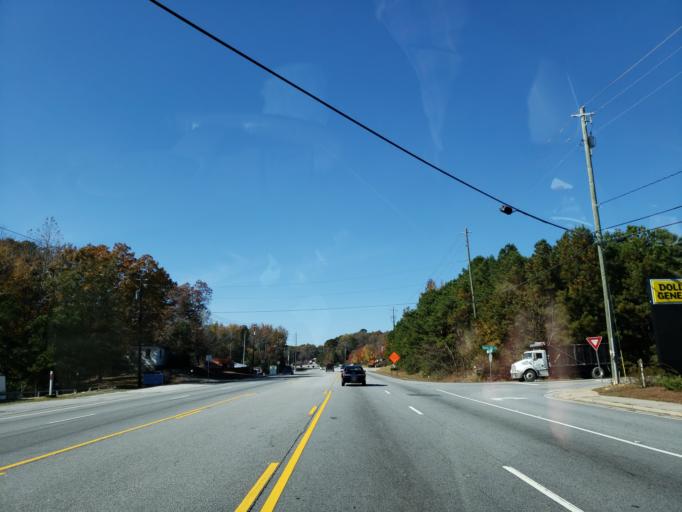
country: US
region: Georgia
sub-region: Cobb County
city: Mableton
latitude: 33.7846
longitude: -84.5421
